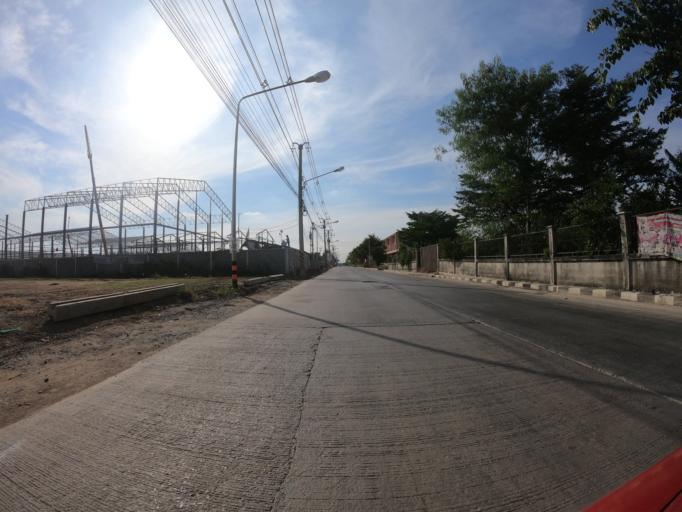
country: TH
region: Pathum Thani
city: Lam Luk Ka
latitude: 13.9612
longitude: 100.7236
